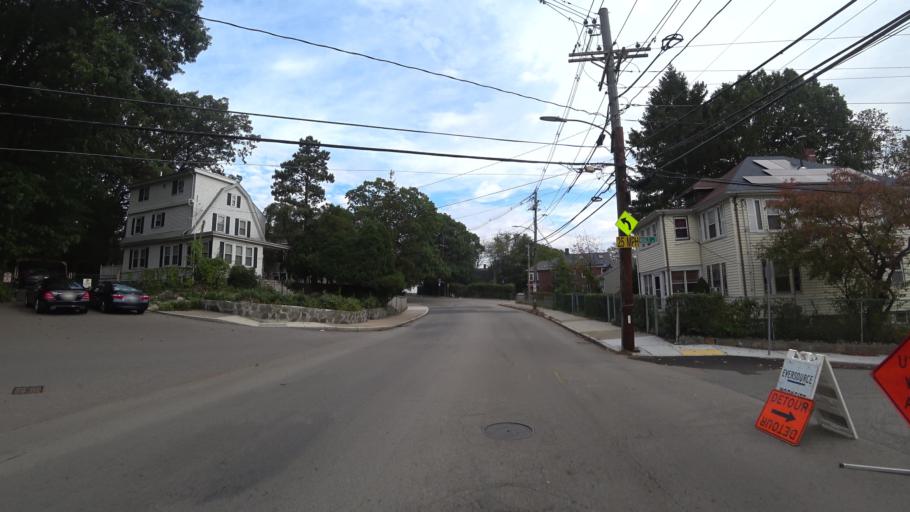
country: US
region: Massachusetts
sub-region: Suffolk County
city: Jamaica Plain
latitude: 42.2702
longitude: -71.1104
